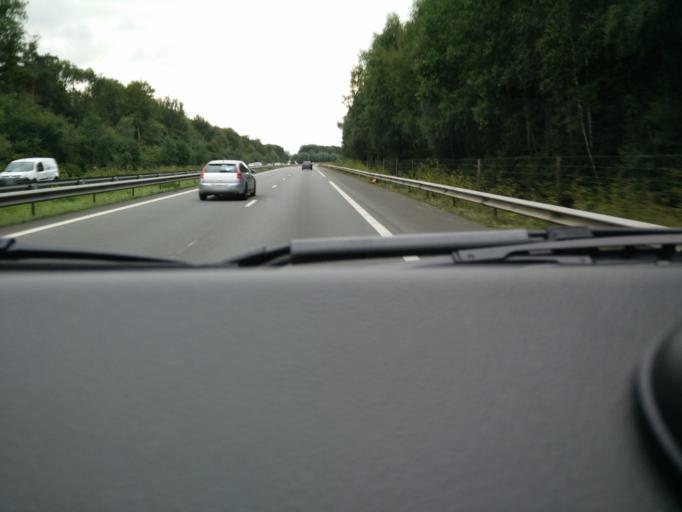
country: FR
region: Nord-Pas-de-Calais
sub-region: Departement du Nord
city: Hasnon
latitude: 50.4142
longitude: 3.4197
